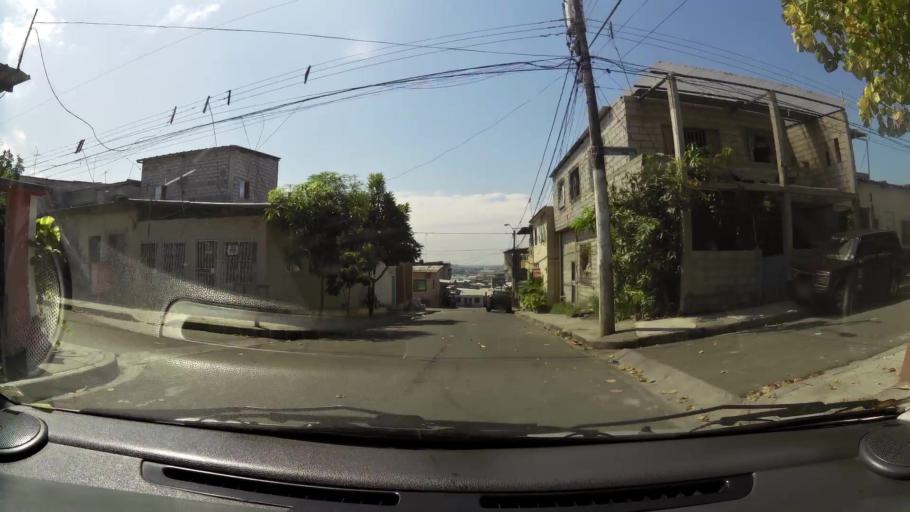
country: EC
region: Guayas
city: Guayaquil
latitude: -2.1281
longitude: -79.9174
